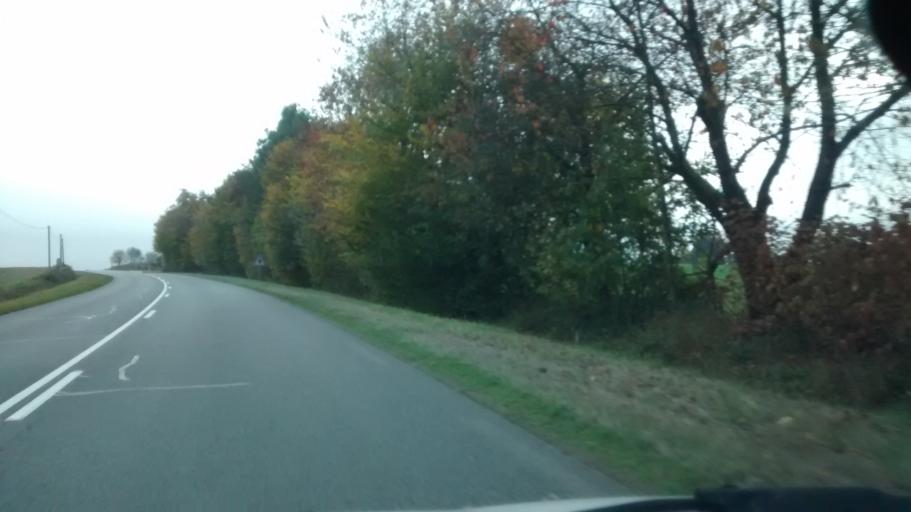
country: FR
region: Brittany
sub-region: Departement d'Ille-et-Vilaine
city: Acigne
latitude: 48.1570
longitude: -1.5174
